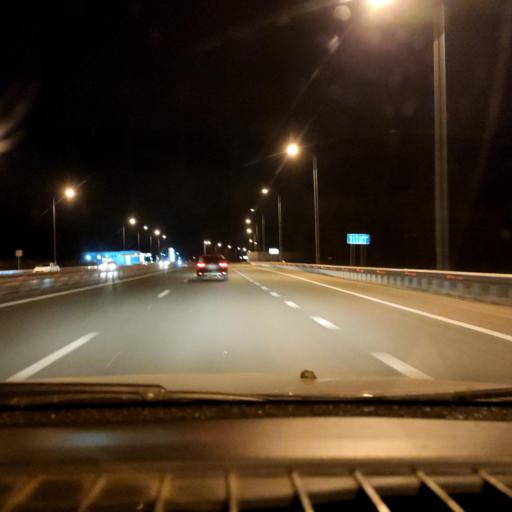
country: RU
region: Samara
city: Bereza
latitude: 53.5081
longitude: 50.1338
